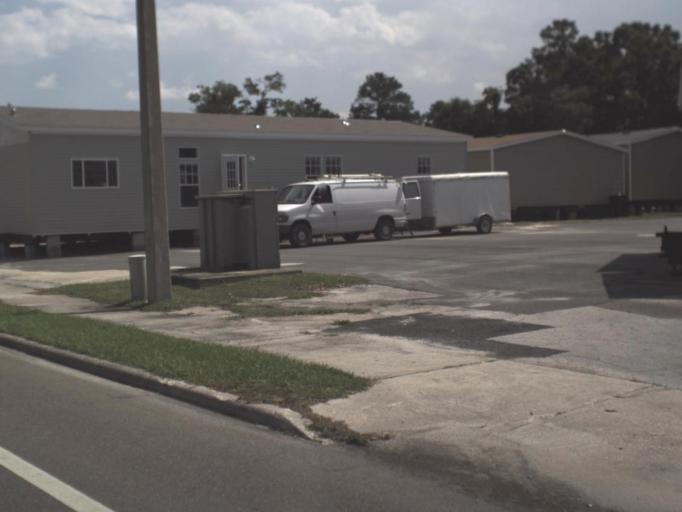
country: US
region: Florida
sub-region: Alachua County
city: Gainesville
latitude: 29.6948
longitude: -82.3389
